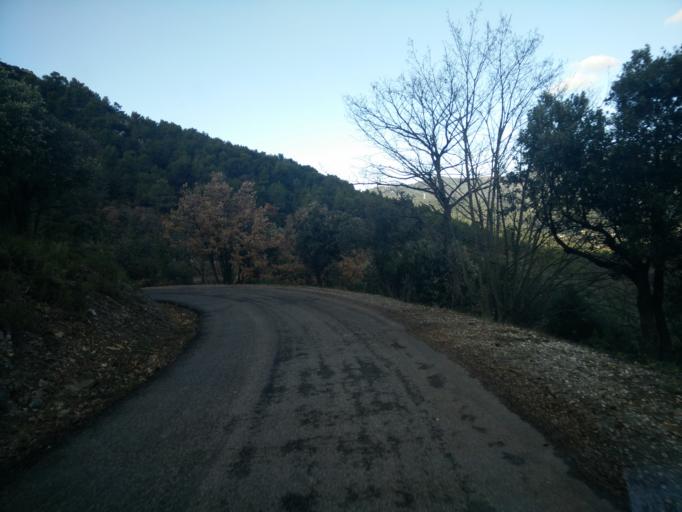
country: FR
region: Provence-Alpes-Cote d'Azur
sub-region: Departement du Var
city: Signes
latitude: 43.2702
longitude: 5.8462
